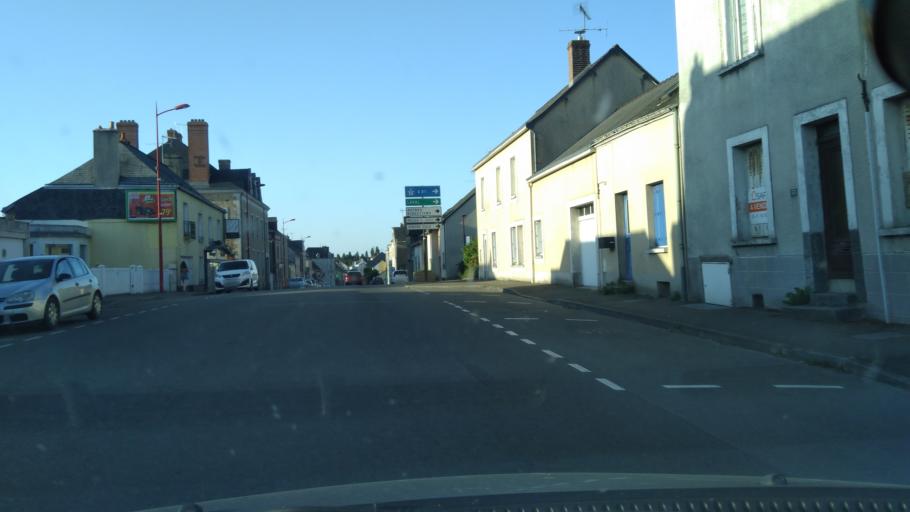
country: FR
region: Pays de la Loire
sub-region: Departement de la Mayenne
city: Cosse-le-Vivien
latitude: 47.9430
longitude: -0.9140
